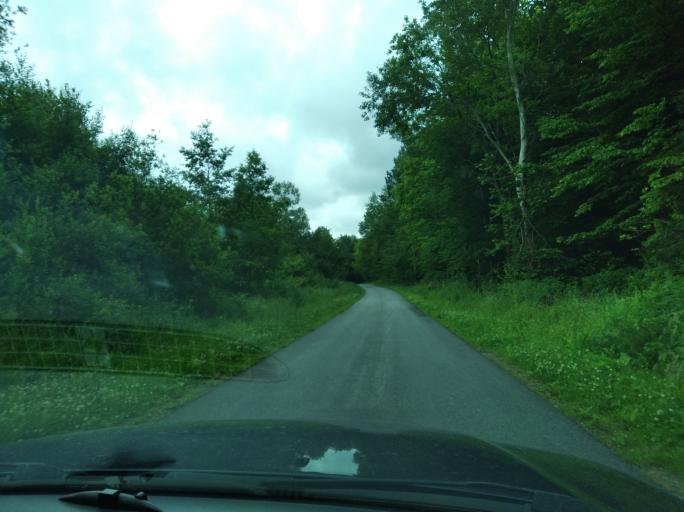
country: PL
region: Subcarpathian Voivodeship
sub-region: Powiat przemyski
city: Przedmiescie Dubieckie
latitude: 49.8750
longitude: 22.4035
